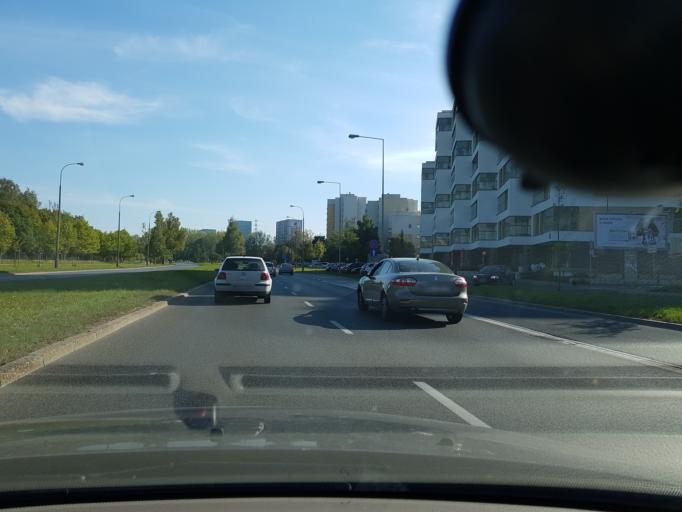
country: PL
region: Masovian Voivodeship
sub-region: Warszawa
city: Ursynow
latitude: 52.1592
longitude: 21.0411
